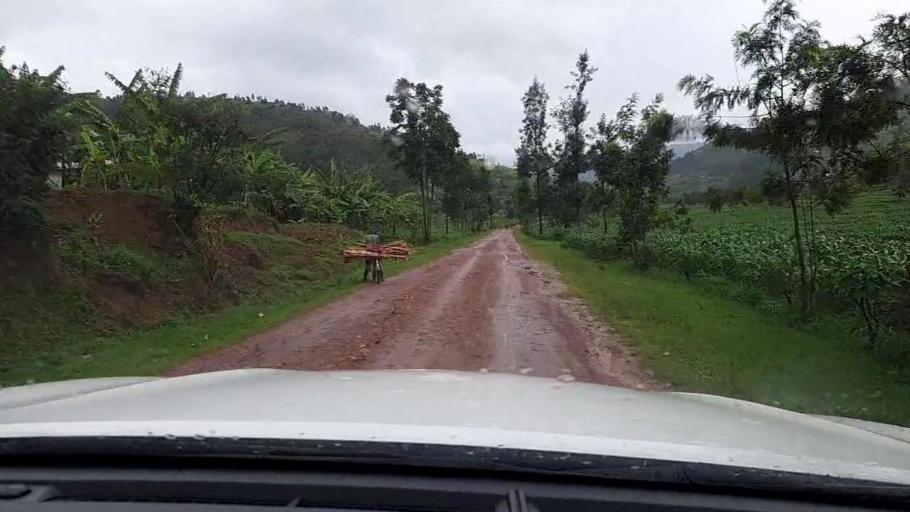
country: RW
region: Northern Province
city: Byumba
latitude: -1.7407
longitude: 29.9436
